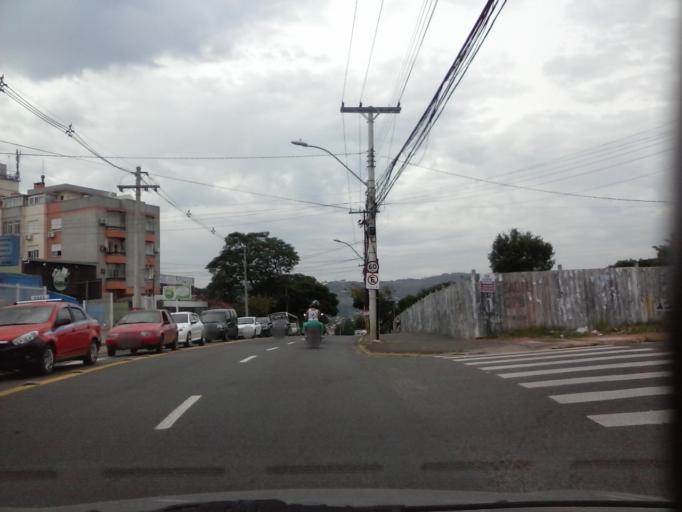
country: BR
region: Rio Grande do Sul
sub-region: Porto Alegre
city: Porto Alegre
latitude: -30.0621
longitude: -51.2064
